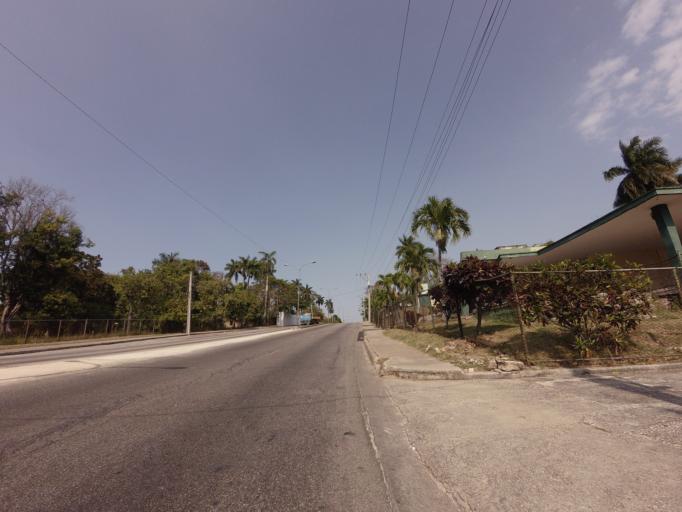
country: CU
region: La Habana
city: Cerro
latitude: 23.0761
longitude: -82.4561
